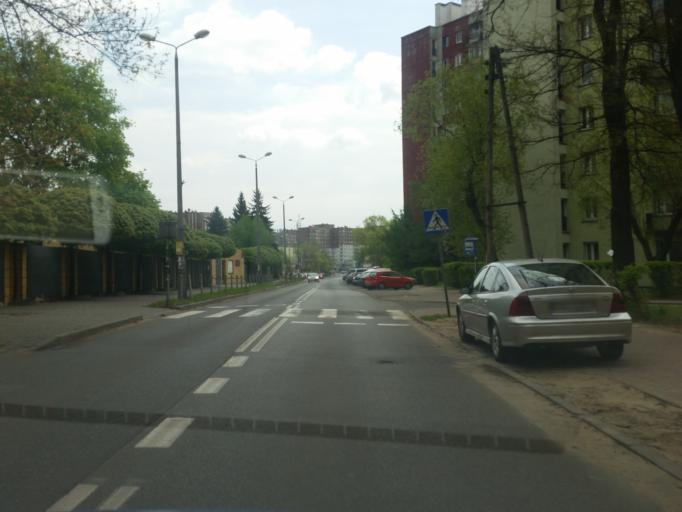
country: PL
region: Silesian Voivodeship
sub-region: Sosnowiec
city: Sosnowiec
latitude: 50.2694
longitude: 19.1295
